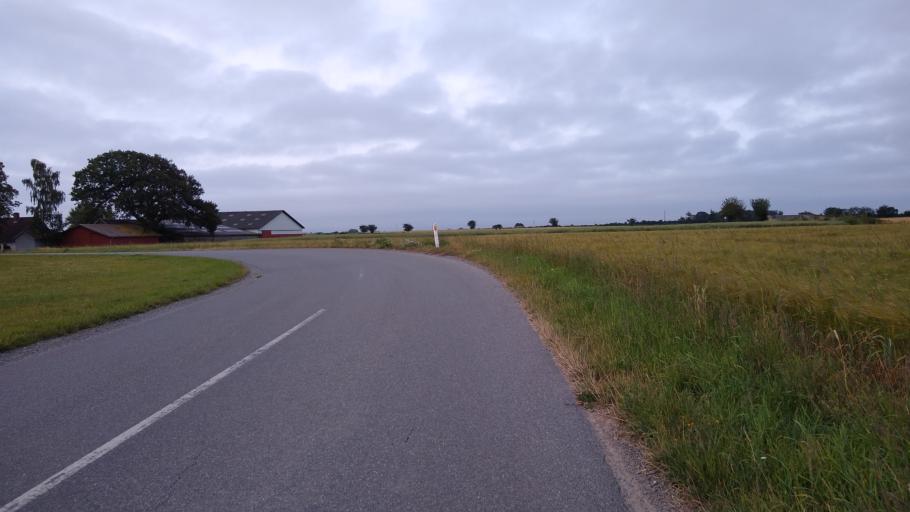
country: DK
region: South Denmark
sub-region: Vejle Kommune
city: Brejning
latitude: 55.6526
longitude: 9.6830
